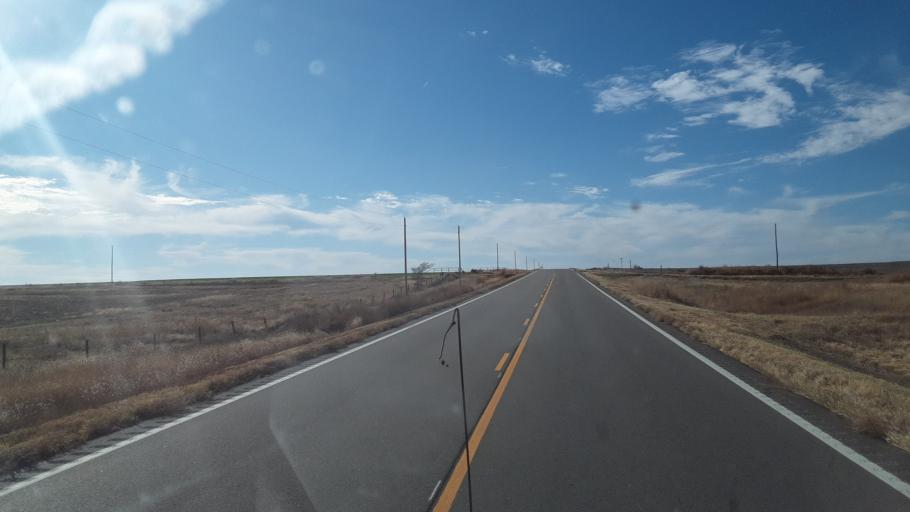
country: US
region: Kansas
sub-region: Hodgeman County
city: Jetmore
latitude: 38.0727
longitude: -100.0255
